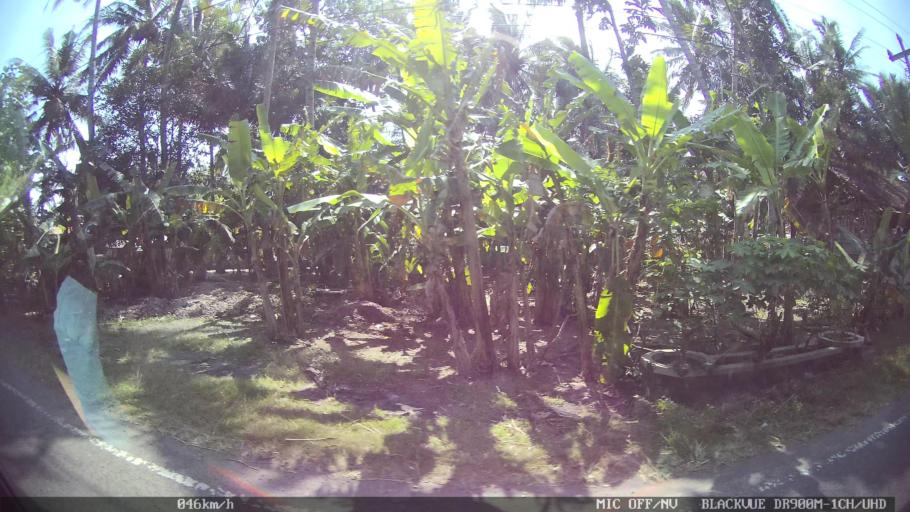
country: ID
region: Daerah Istimewa Yogyakarta
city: Srandakan
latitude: -7.9174
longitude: 110.1551
